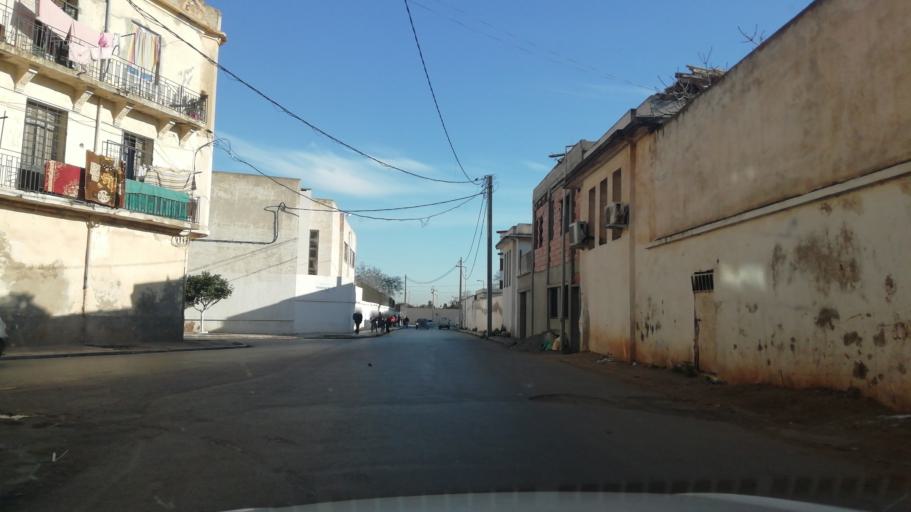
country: DZ
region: Oran
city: Oran
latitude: 35.6944
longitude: -0.6386
